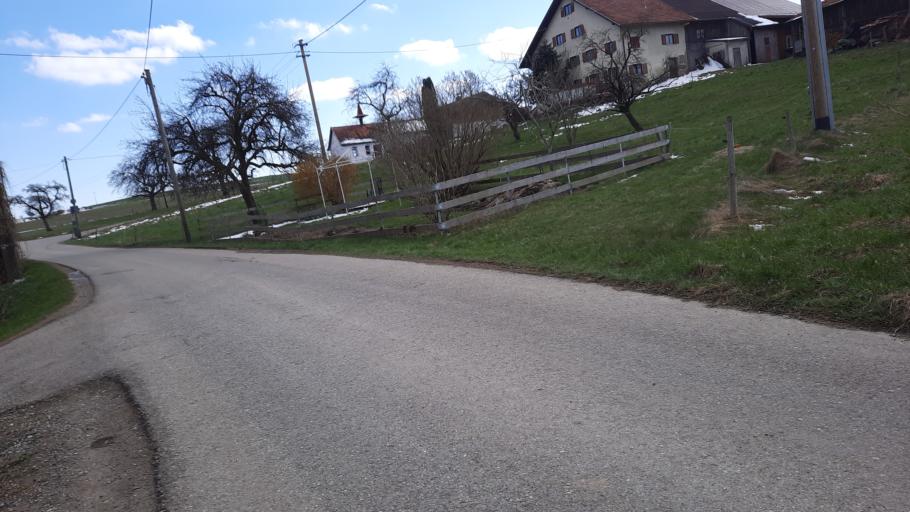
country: DE
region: Bavaria
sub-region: Swabia
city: Altusried
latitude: 47.8178
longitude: 10.2126
